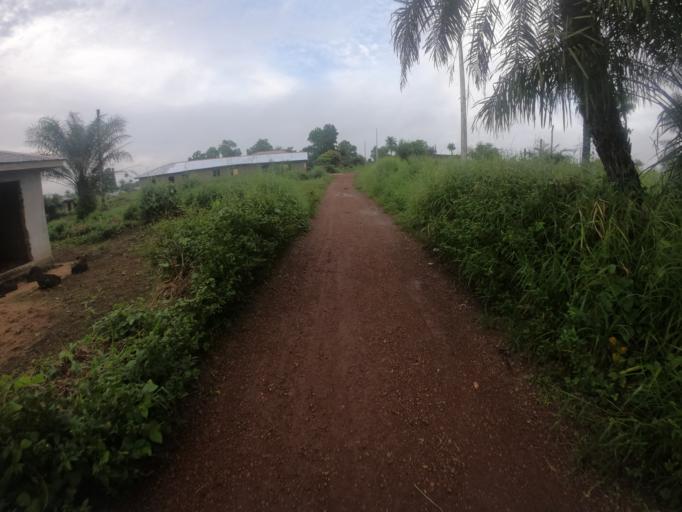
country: SL
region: Northern Province
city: Port Loko
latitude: 8.4971
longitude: -12.7510
